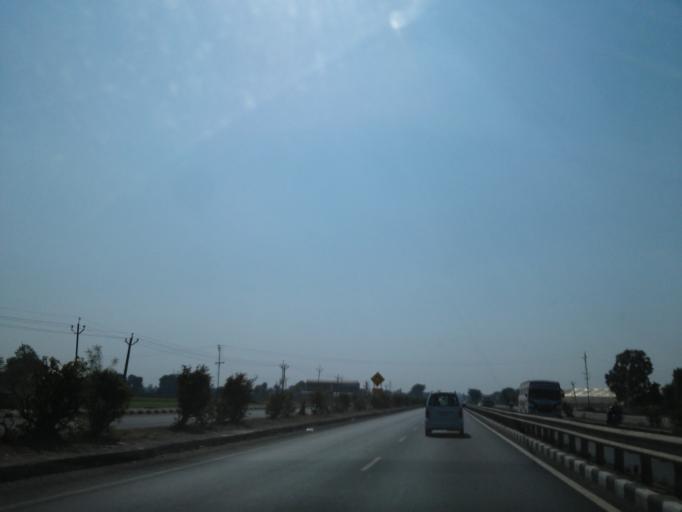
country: IN
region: Gujarat
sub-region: Gandhinagar
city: Chhala
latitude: 23.2489
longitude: 72.7422
